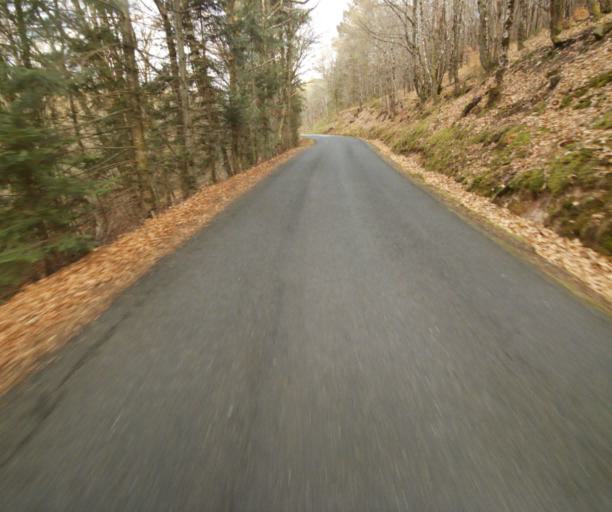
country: FR
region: Limousin
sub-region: Departement de la Correze
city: Correze
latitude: 45.4160
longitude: 1.9032
